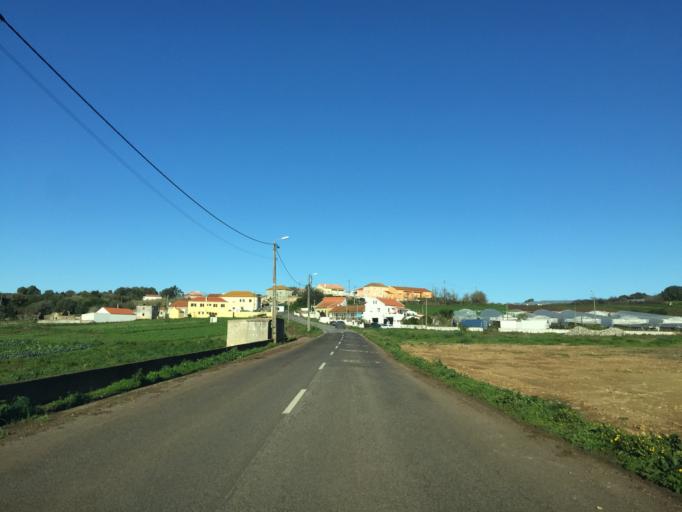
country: PT
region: Lisbon
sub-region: Sintra
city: Almargem
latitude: 38.8661
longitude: -9.2830
